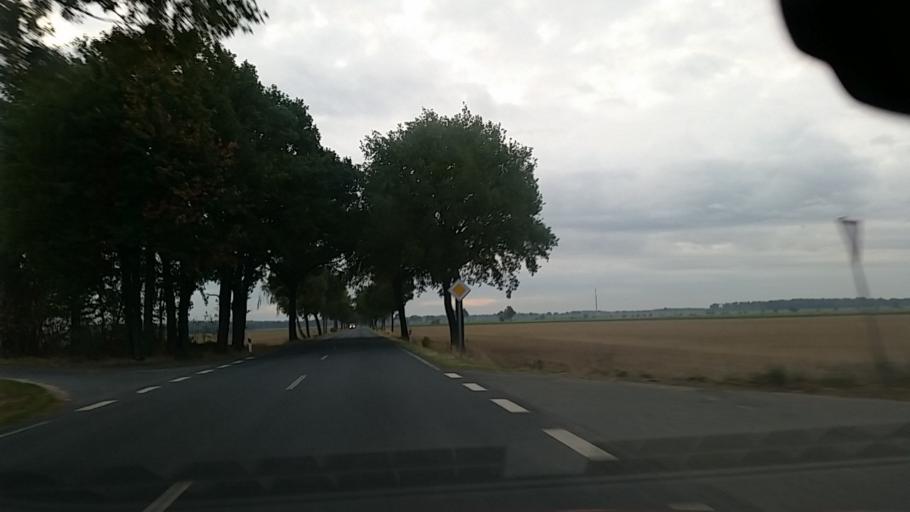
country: DE
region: Lower Saxony
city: Hankensbuttel
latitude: 52.7414
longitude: 10.5680
